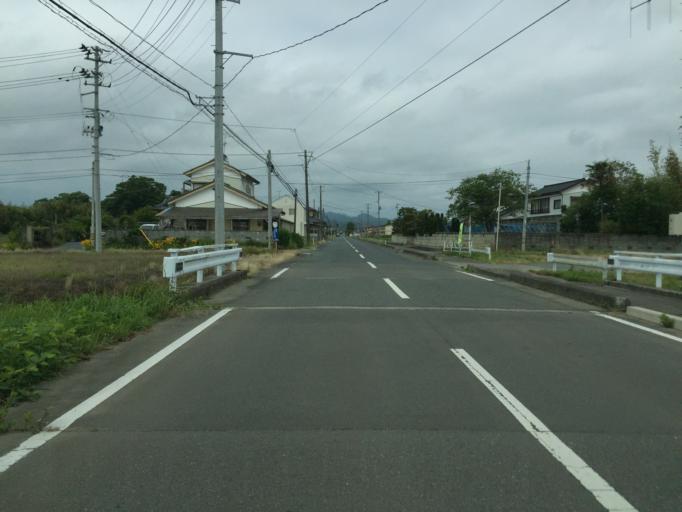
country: JP
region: Fukushima
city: Namie
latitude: 37.6997
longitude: 140.9804
